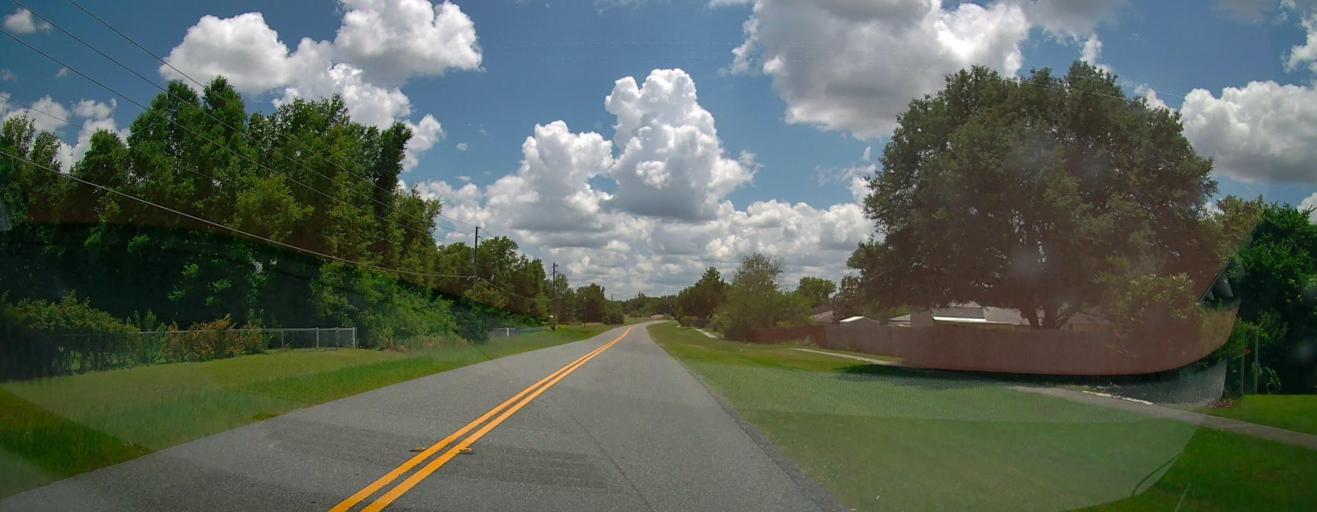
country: US
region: Florida
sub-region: Marion County
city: Silver Springs Shores
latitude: 29.1429
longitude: -82.0385
